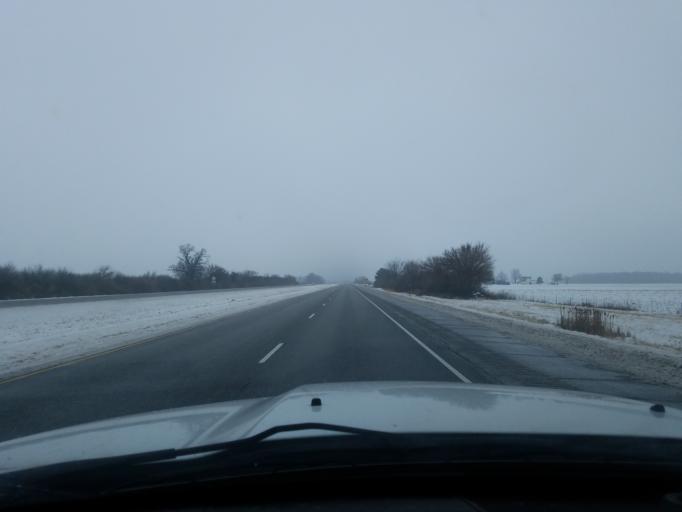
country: US
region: Indiana
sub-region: Fulton County
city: Rochester
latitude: 40.9842
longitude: -86.1679
